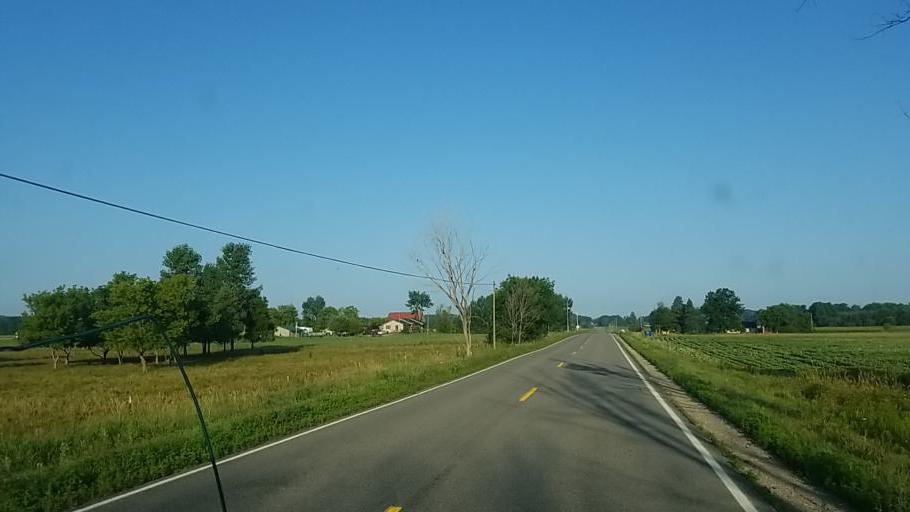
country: US
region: Michigan
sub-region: Montcalm County
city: Howard City
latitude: 43.3666
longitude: -85.4885
